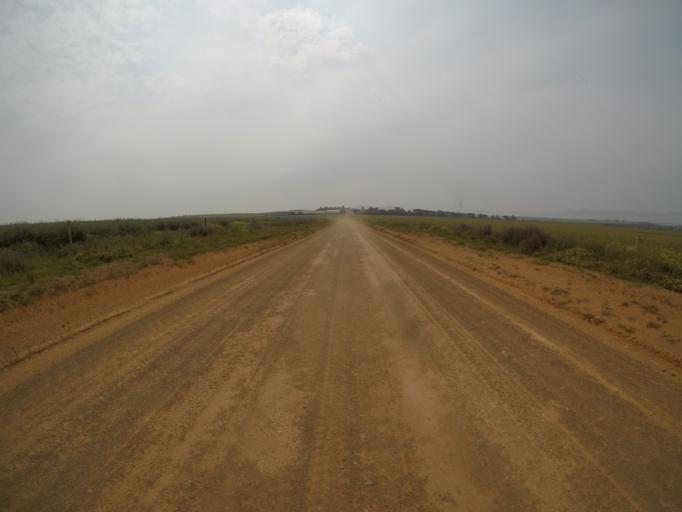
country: ZA
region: Western Cape
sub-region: City of Cape Town
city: Kraaifontein
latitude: -33.7113
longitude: 18.6867
